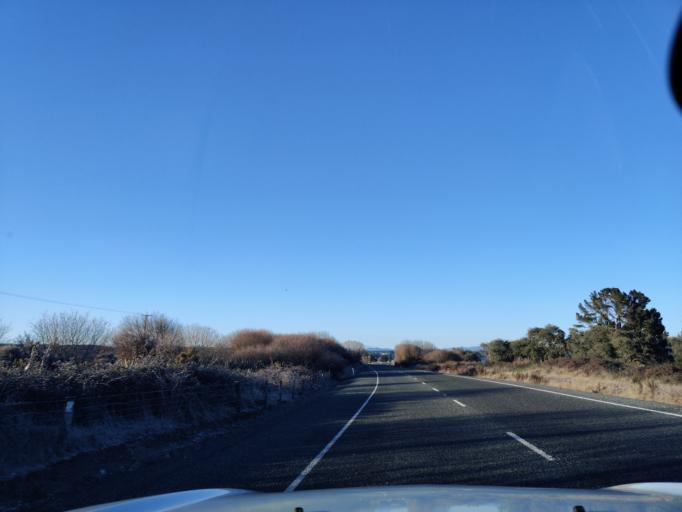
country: NZ
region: Waikato
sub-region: Taupo District
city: Taupo
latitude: -38.7628
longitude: 176.0753
